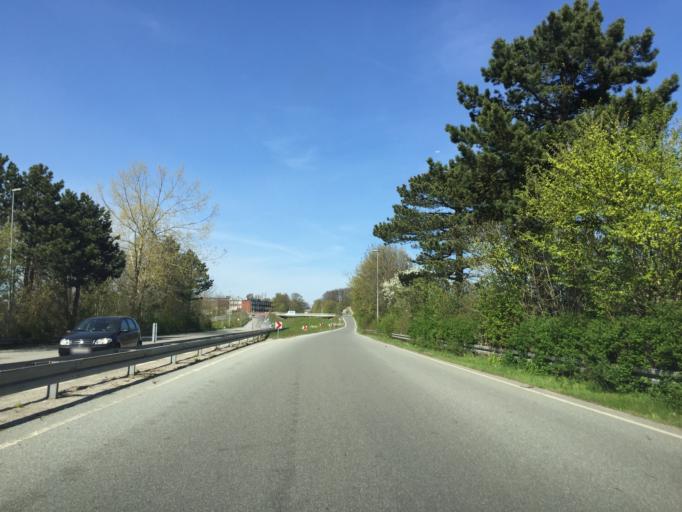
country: DK
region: Capital Region
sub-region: Gladsaxe Municipality
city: Buddinge
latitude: 55.7270
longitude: 12.5001
